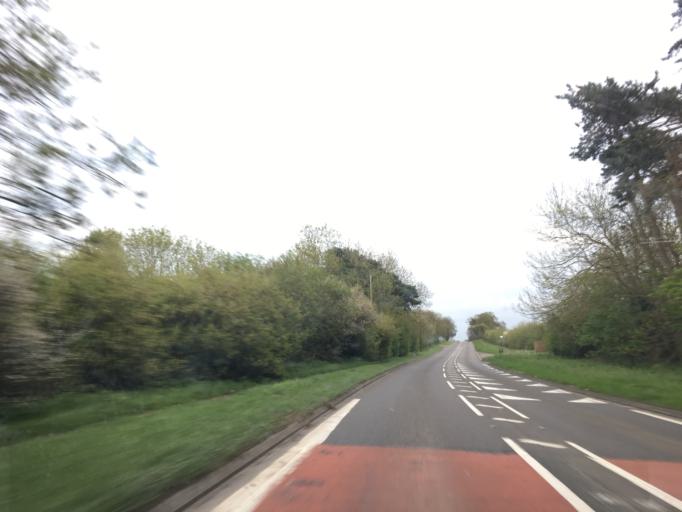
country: GB
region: England
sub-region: Leicestershire
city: Houghton on the Hill
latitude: 52.6302
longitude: -1.0260
